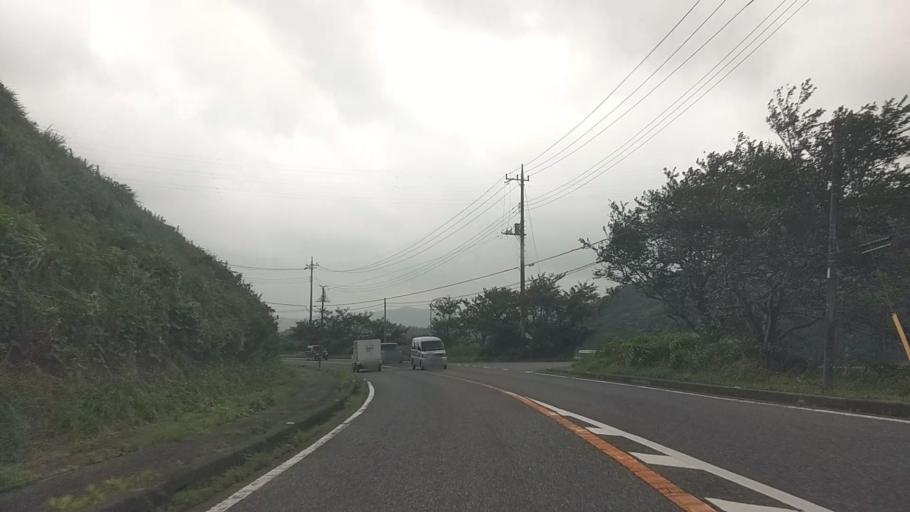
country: JP
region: Chiba
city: Kawaguchi
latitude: 35.1421
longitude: 140.0689
